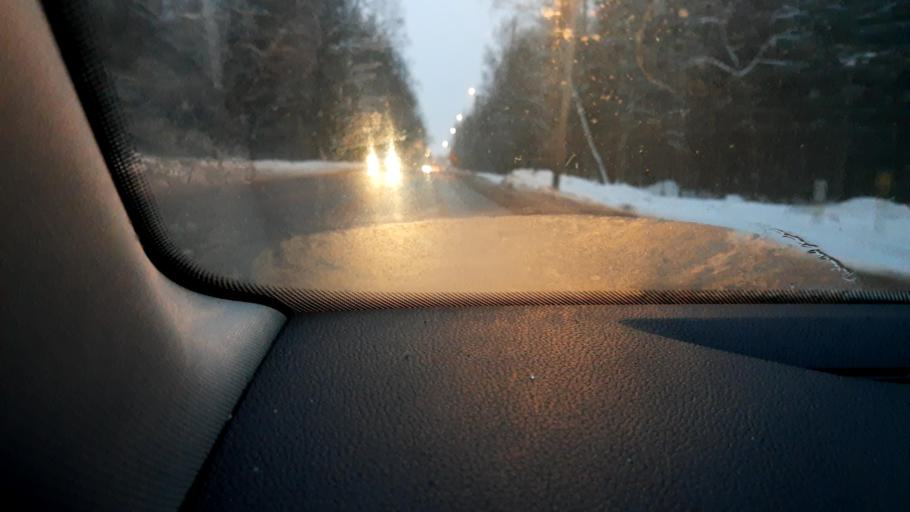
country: RU
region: Moskovskaya
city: Troitsk
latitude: 55.3127
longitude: 37.1668
